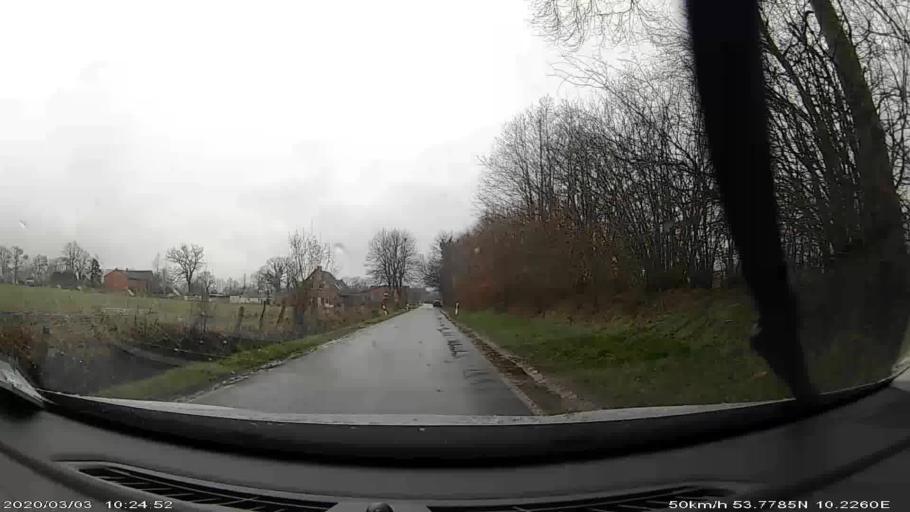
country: DE
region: Schleswig-Holstein
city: Sulfeld
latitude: 53.7798
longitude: 10.2214
